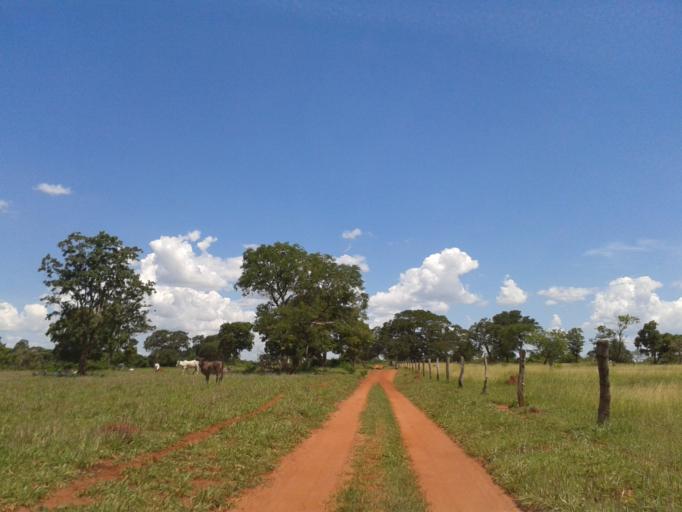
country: BR
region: Minas Gerais
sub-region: Santa Vitoria
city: Santa Vitoria
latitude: -19.1320
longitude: -50.5568
